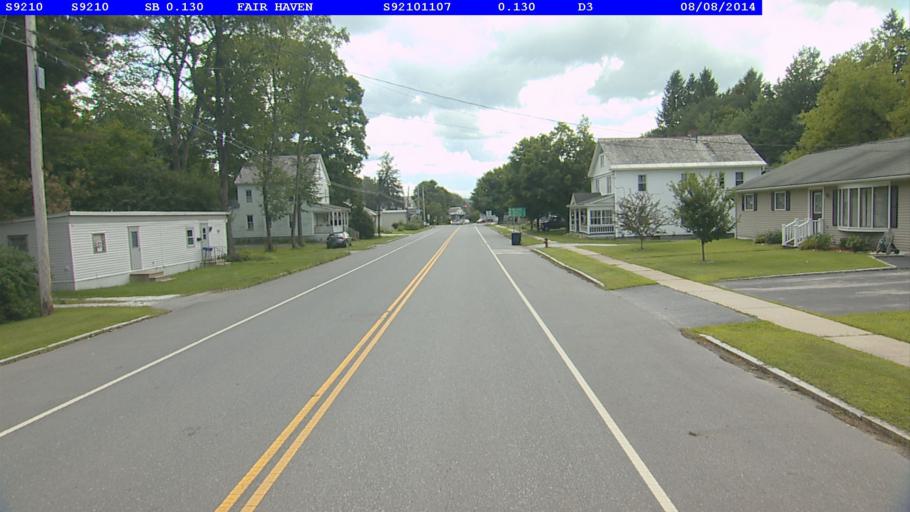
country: US
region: Vermont
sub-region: Rutland County
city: Fair Haven
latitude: 43.6013
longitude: -73.2615
